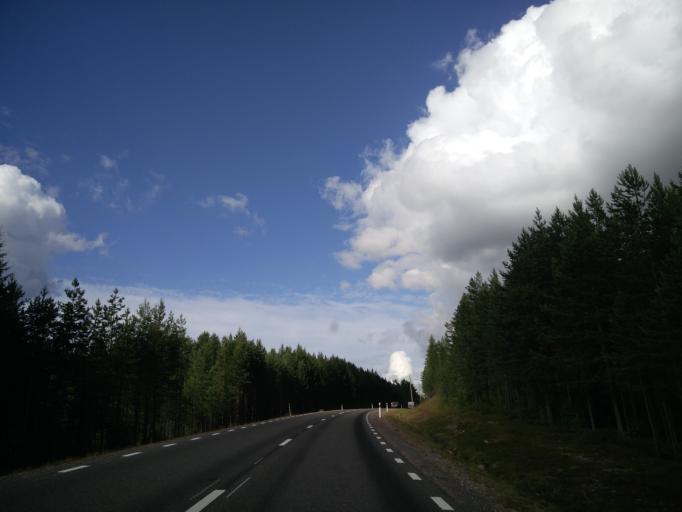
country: SE
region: Vaermland
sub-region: Torsby Kommun
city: Torsby
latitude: 60.3721
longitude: 13.2065
